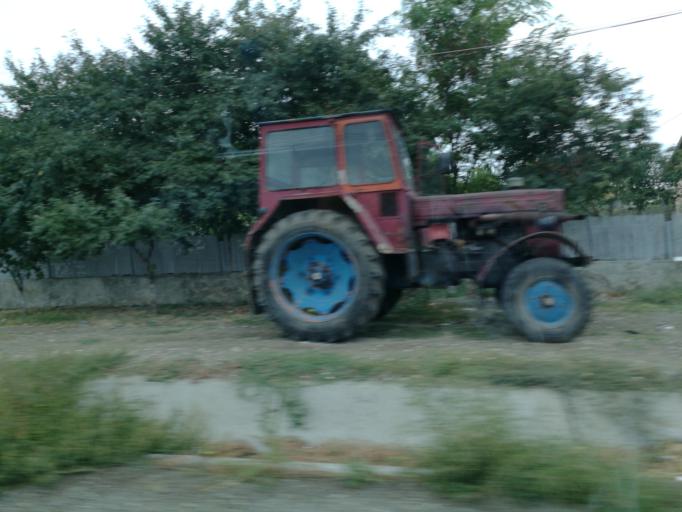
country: RO
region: Constanta
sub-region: Comuna Cogealac
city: Tariverde
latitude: 44.5543
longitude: 28.6028
